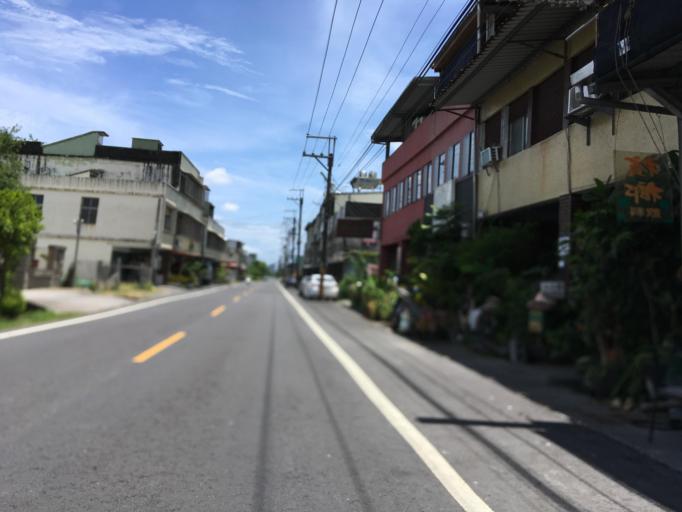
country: TW
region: Taiwan
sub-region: Yilan
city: Yilan
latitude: 24.6578
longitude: 121.7328
